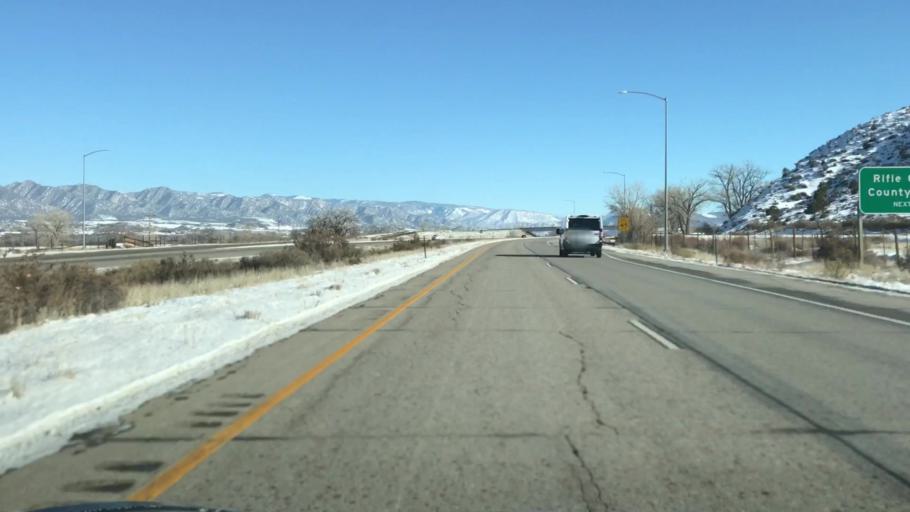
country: US
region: Colorado
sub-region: Garfield County
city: Rifle
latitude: 39.5313
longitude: -107.7195
